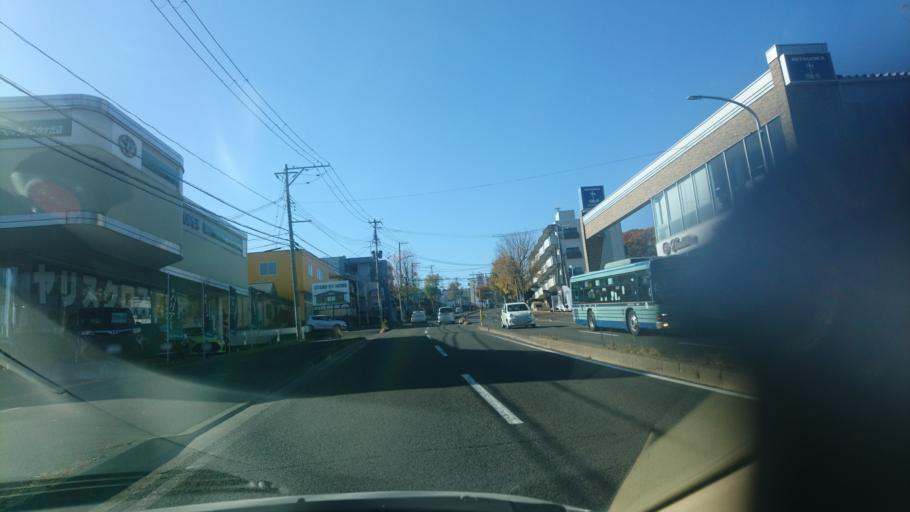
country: JP
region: Miyagi
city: Sendai-shi
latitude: 38.3086
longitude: 140.8420
